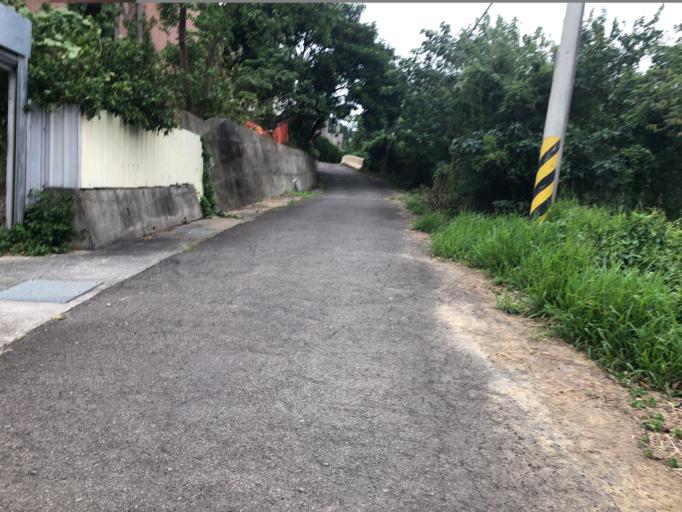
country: TW
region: Taiwan
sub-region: Hsinchu
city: Hsinchu
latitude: 24.7550
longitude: 120.9475
